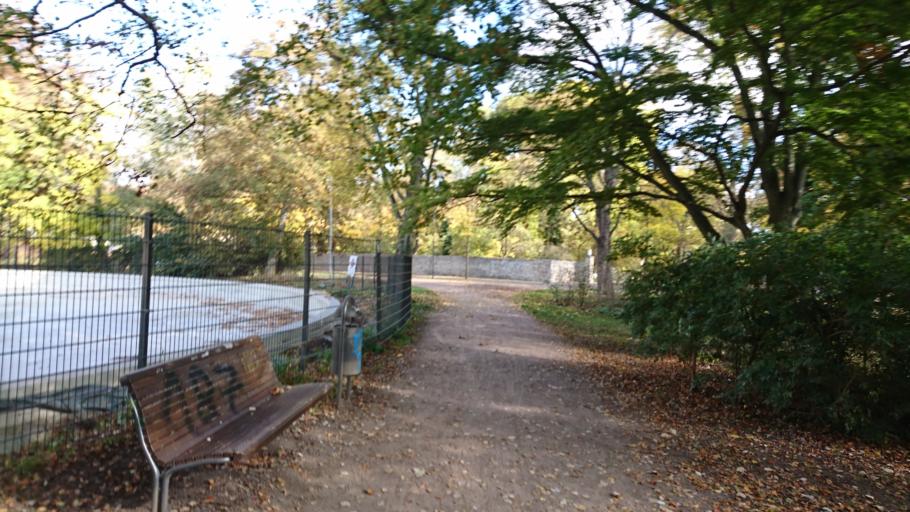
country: DE
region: Thuringia
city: Weimar
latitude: 50.9840
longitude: 11.3203
